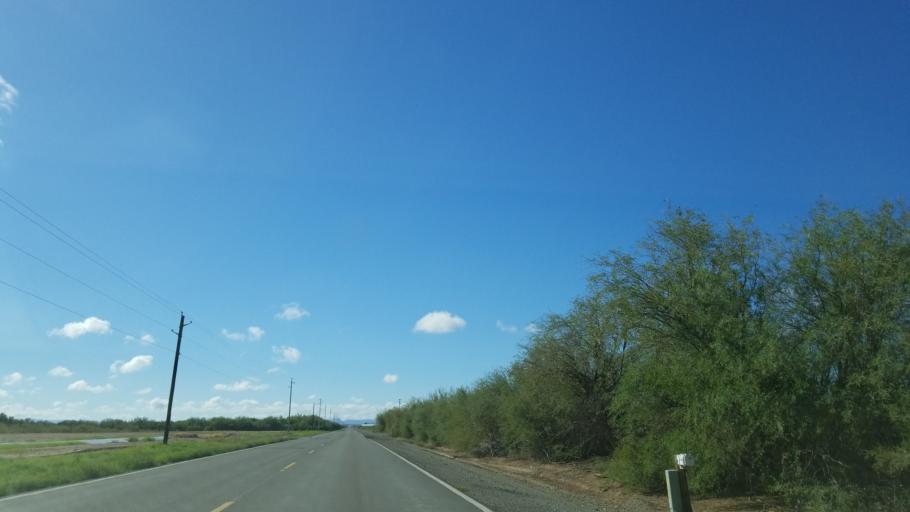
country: US
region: Arizona
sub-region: La Paz County
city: Salome
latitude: 33.6619
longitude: -113.7673
